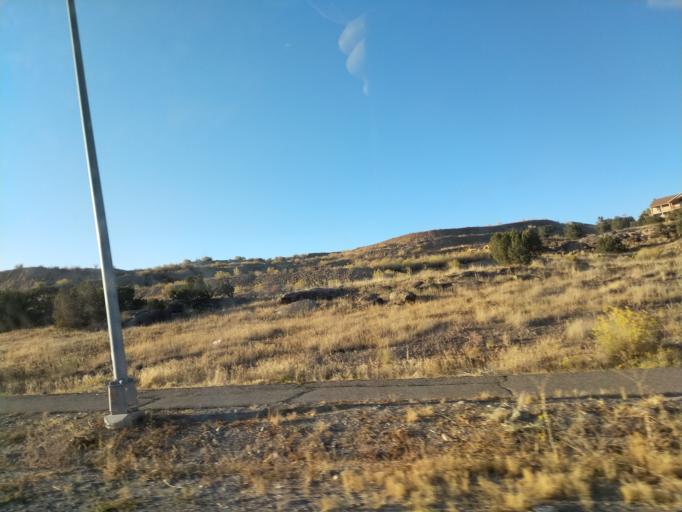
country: US
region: Colorado
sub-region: Mesa County
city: Redlands
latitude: 39.0570
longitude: -108.6145
